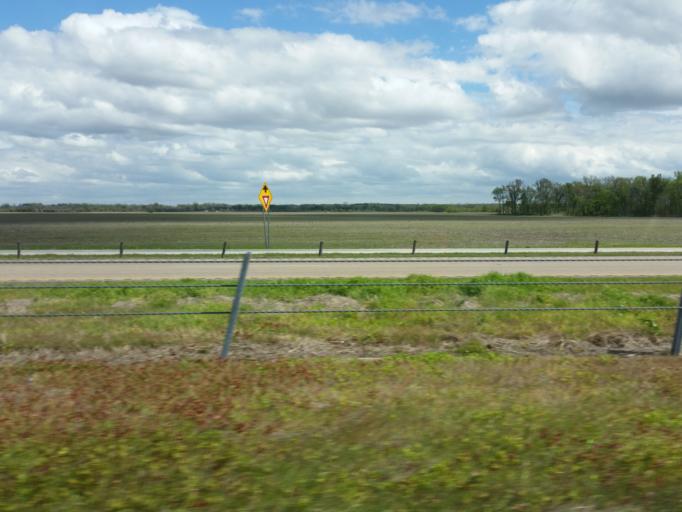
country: US
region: Arkansas
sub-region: Crittenden County
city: Marion
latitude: 35.3621
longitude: -90.2798
